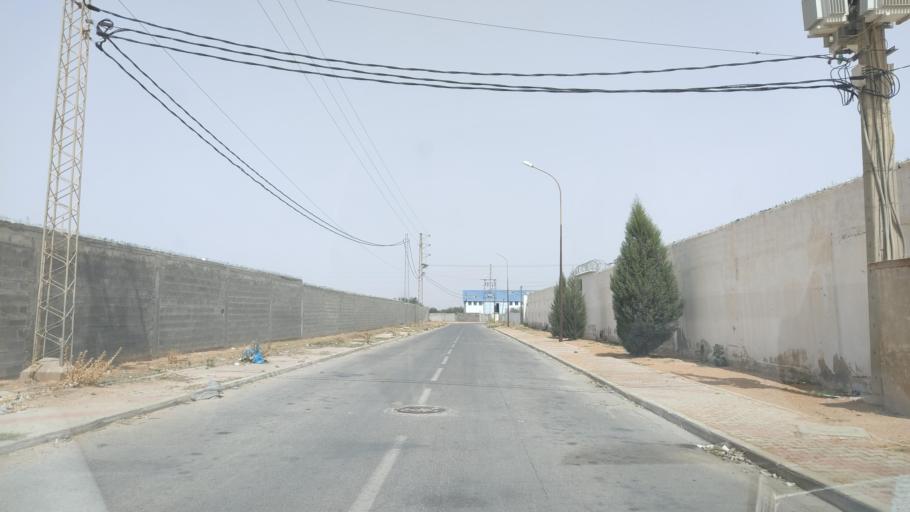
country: TN
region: Al Mahdiyah
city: El Jem
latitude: 35.1299
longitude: 10.7365
